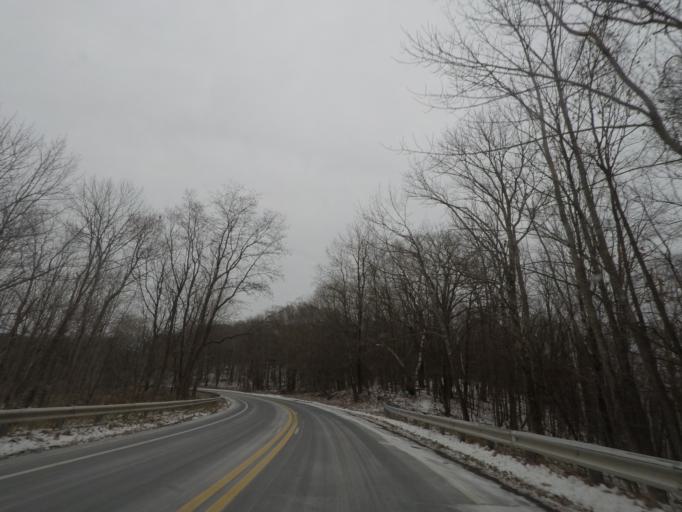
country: US
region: Massachusetts
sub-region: Berkshire County
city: Williamstown
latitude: 42.7086
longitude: -73.2525
